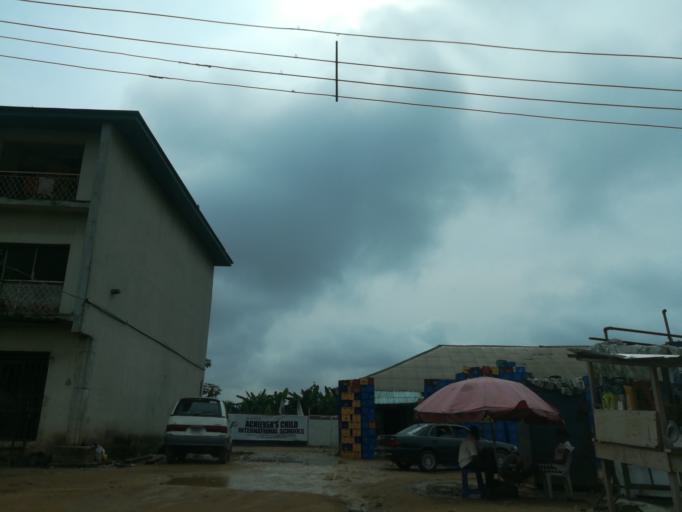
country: NG
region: Rivers
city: Port Harcourt
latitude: 4.8775
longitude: 6.9811
